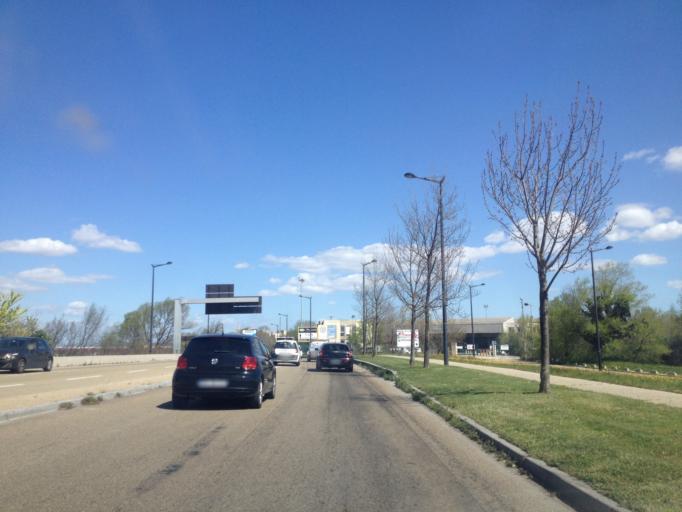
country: FR
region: Provence-Alpes-Cote d'Azur
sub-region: Departement du Vaucluse
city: Avignon
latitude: 43.9409
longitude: 4.7906
